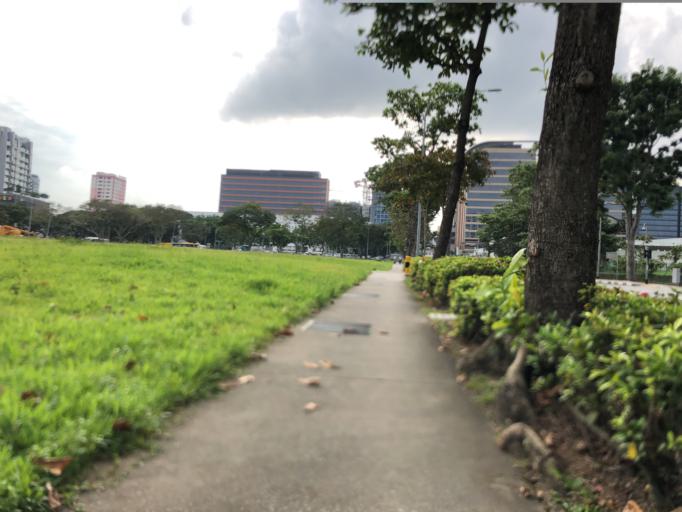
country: SG
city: Singapore
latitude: 1.3175
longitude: 103.8973
